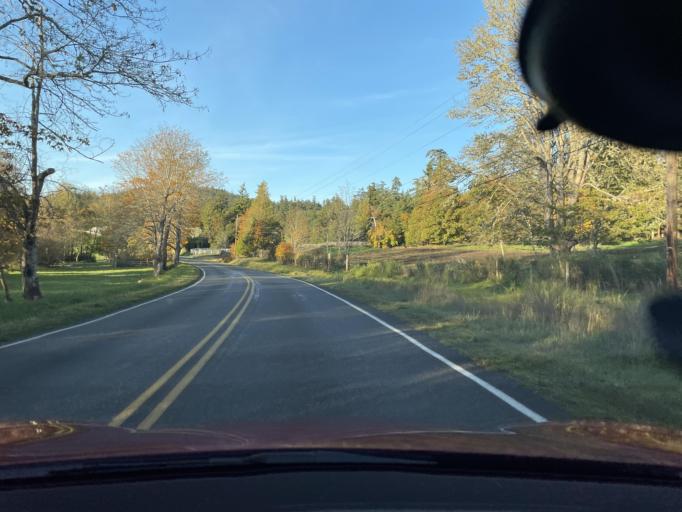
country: US
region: Washington
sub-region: San Juan County
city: Friday Harbor
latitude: 48.5704
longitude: -123.1392
